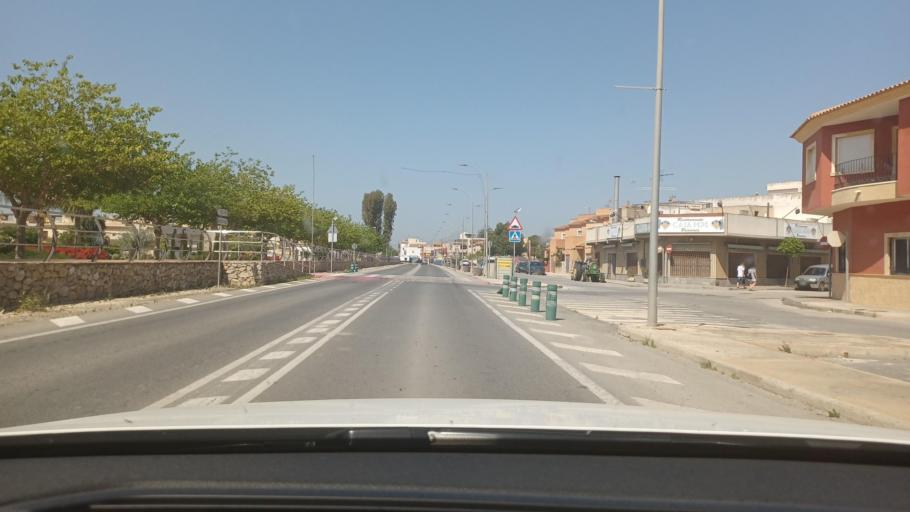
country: ES
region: Valencia
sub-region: Provincia de Alicante
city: Dolores
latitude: 38.1379
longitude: -0.7647
